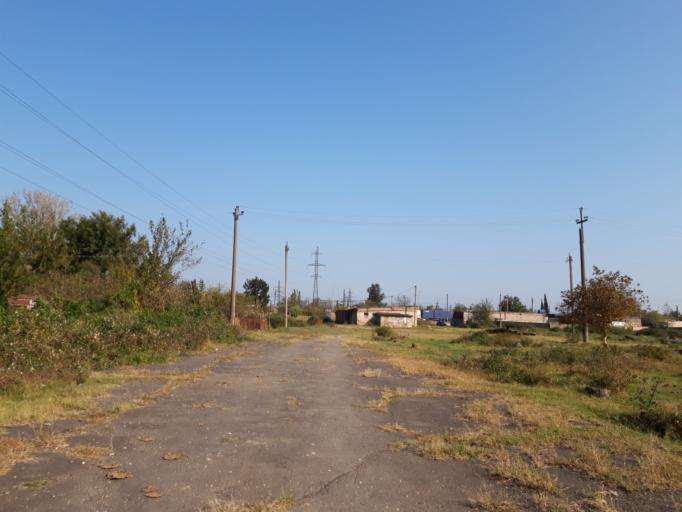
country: GE
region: Imereti
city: Samtredia
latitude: 42.1577
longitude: 42.3247
